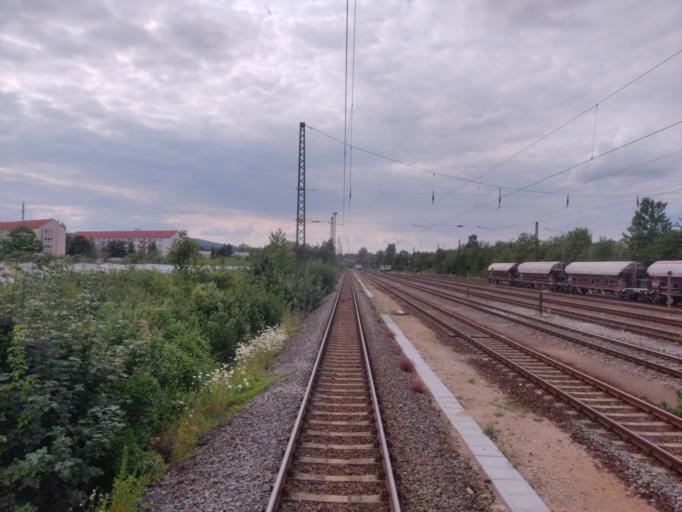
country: DE
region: Saxony-Anhalt
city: Blankenburg
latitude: 51.8061
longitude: 10.9499
